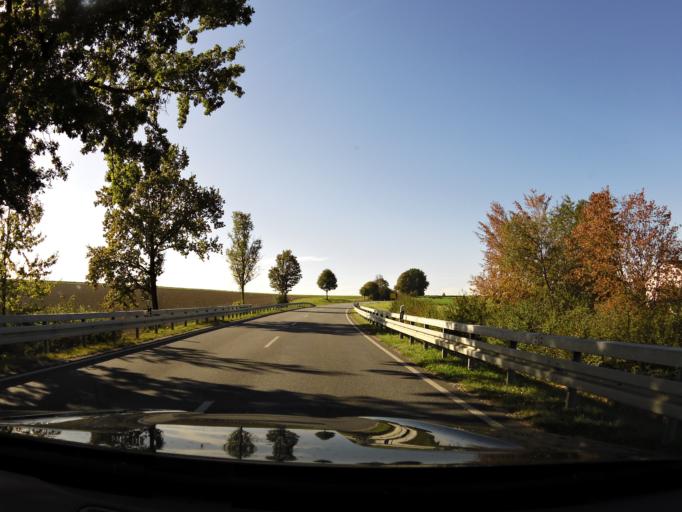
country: DE
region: Bavaria
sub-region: Lower Bavaria
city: Altfraunhofen
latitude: 48.4492
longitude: 12.1492
